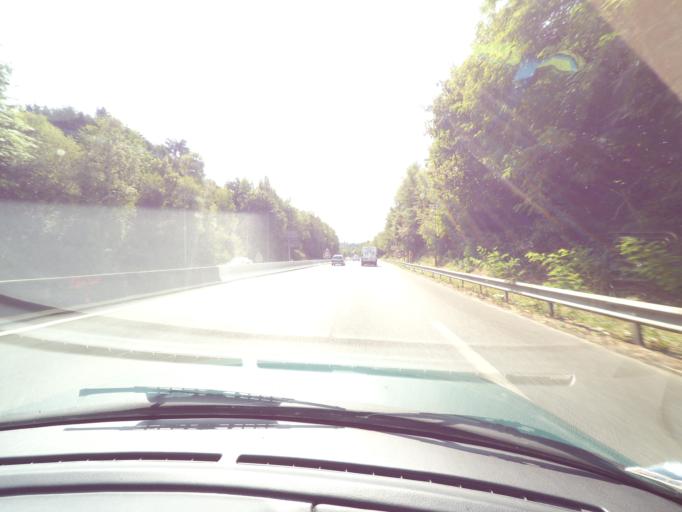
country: FR
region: Limousin
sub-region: Departement de la Haute-Vienne
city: Limoges
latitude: 45.8265
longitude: 1.2842
